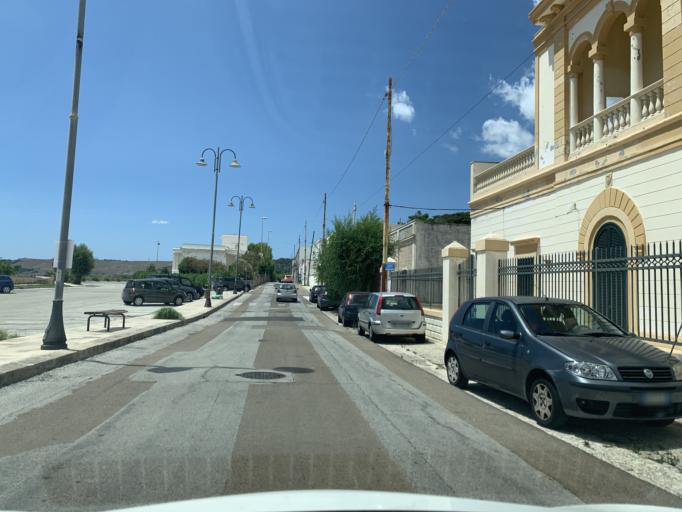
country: IT
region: Apulia
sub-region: Provincia di Lecce
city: Santa Cesarea Terme
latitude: 40.0359
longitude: 18.4597
